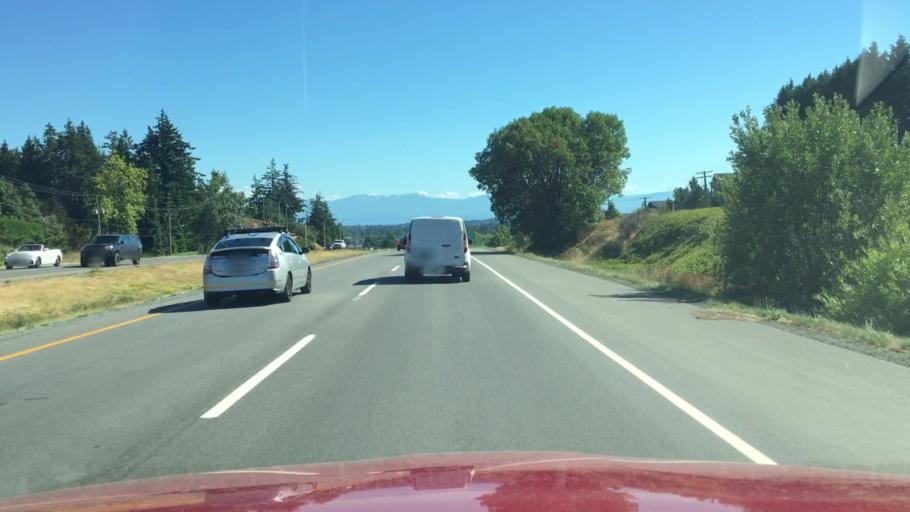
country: CA
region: British Columbia
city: Victoria
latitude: 48.5061
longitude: -123.3849
